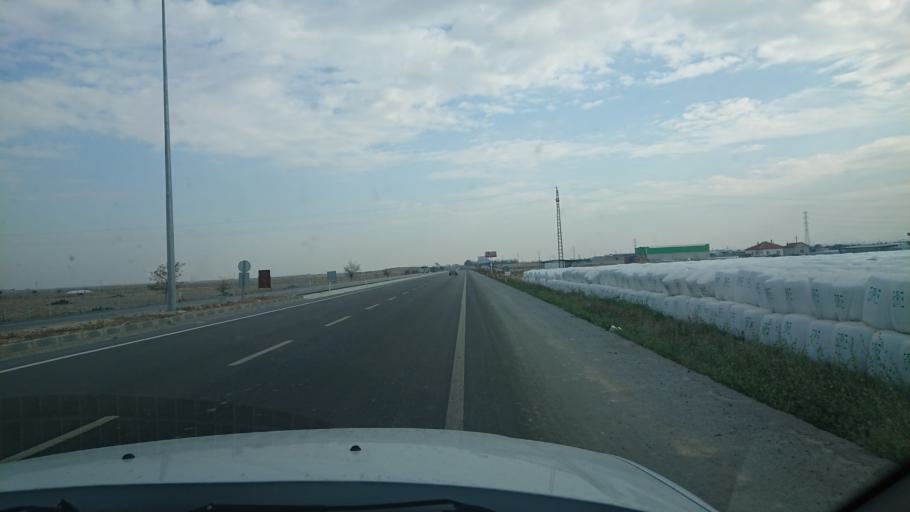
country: TR
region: Aksaray
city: Yesilova
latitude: 38.2930
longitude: 33.7684
